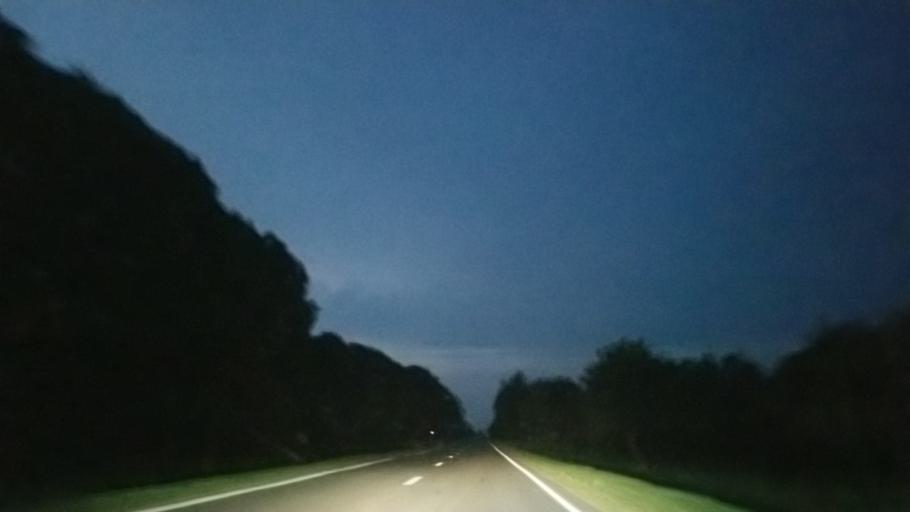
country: PL
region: Lublin Voivodeship
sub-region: Powiat bialski
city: Koden
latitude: 51.9099
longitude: 23.6566
